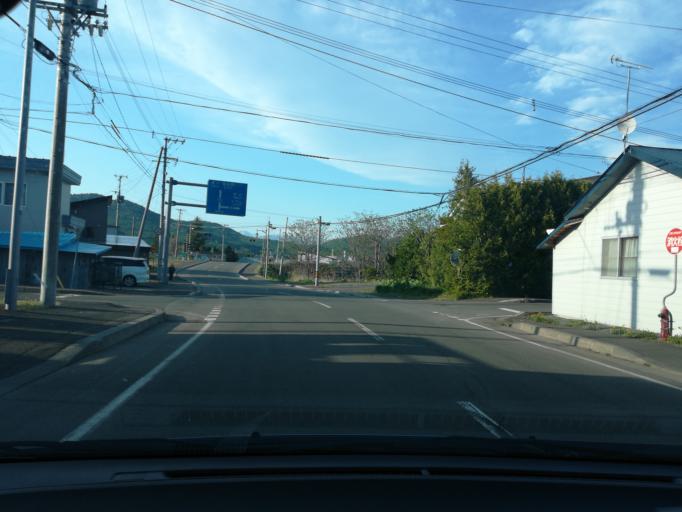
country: JP
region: Hokkaido
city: Shimo-furano
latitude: 43.1608
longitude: 142.5672
